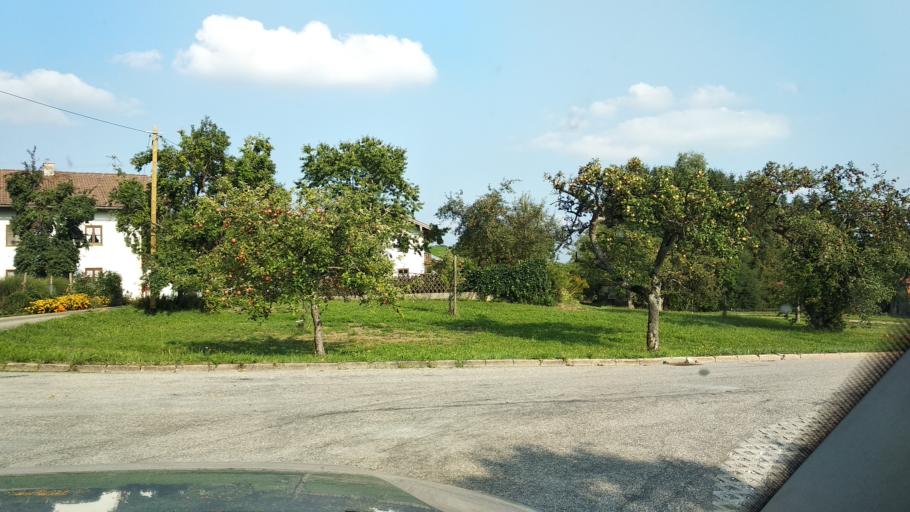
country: DE
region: Bavaria
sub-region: Upper Bavaria
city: Ebersberg
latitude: 48.0986
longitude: 11.9865
